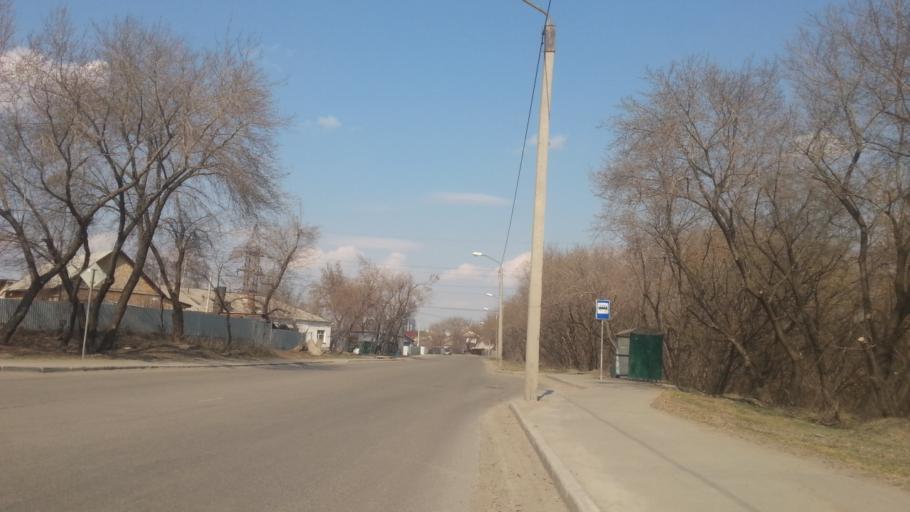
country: RU
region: Altai Krai
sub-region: Gorod Barnaulskiy
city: Barnaul
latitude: 53.3203
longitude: 83.7630
